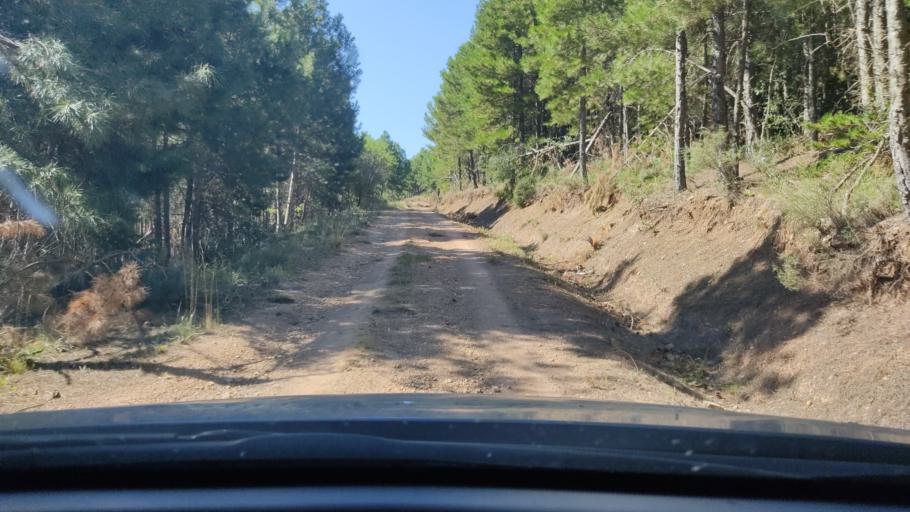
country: ES
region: Aragon
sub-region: Provincia de Teruel
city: Monforte de Moyuela
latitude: 41.0328
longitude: -1.0477
